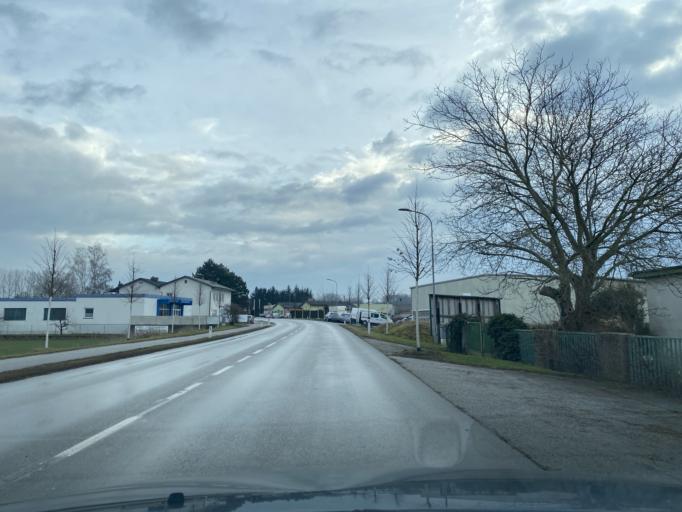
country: AT
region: Lower Austria
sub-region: Politischer Bezirk Sankt Polten
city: Prinzersdorf
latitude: 48.1998
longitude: 15.5049
